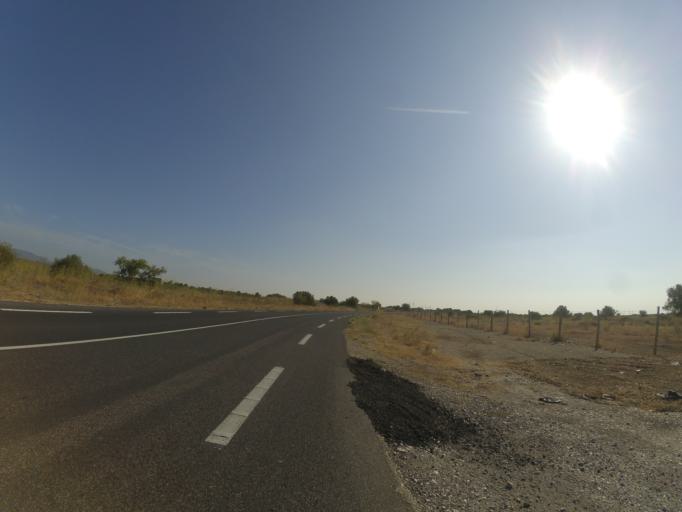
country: FR
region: Languedoc-Roussillon
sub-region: Departement des Pyrenees-Orientales
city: Rivesaltes
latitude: 42.7977
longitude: 2.8612
